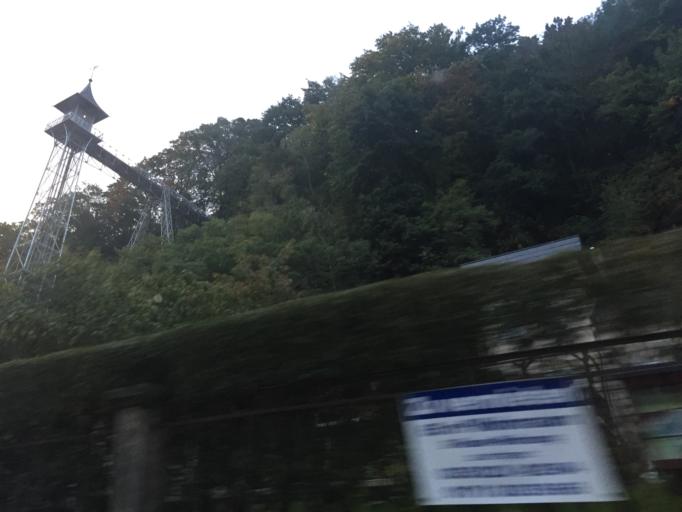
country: DE
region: Saxony
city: Bad Schandau
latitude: 50.9163
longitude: 14.1619
